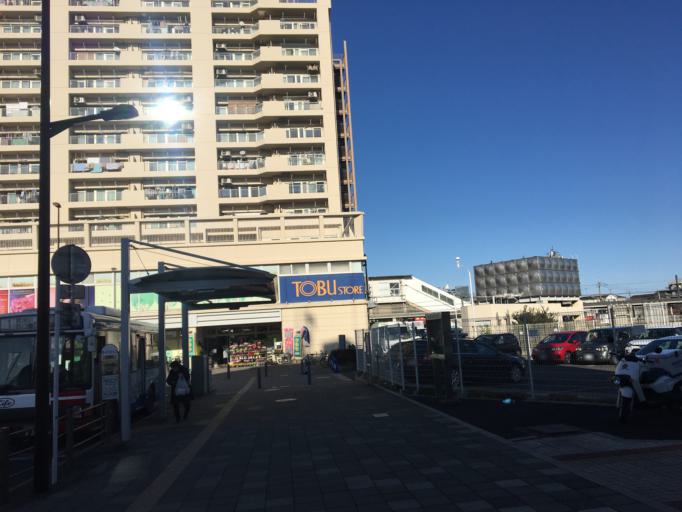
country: JP
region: Saitama
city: Oi
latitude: 35.8452
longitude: 139.5387
